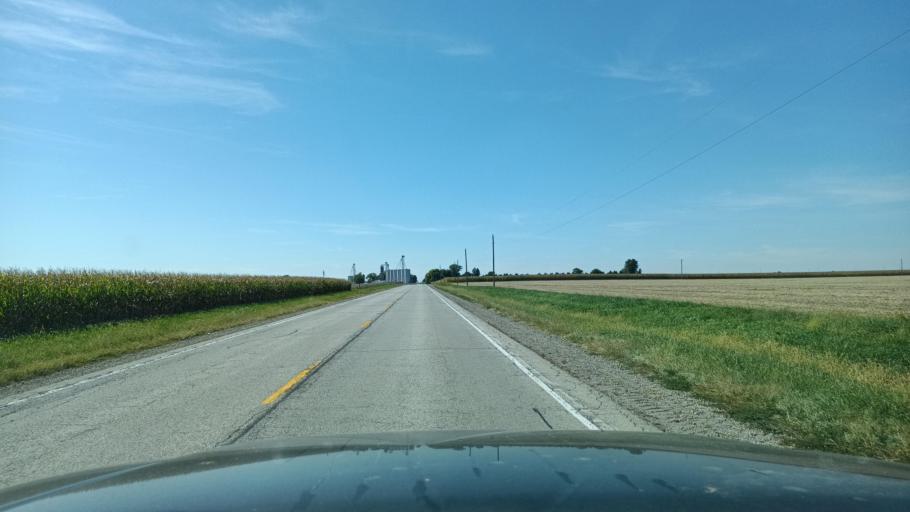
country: US
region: Illinois
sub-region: De Witt County
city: Farmer City
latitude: 40.2238
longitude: -88.7047
